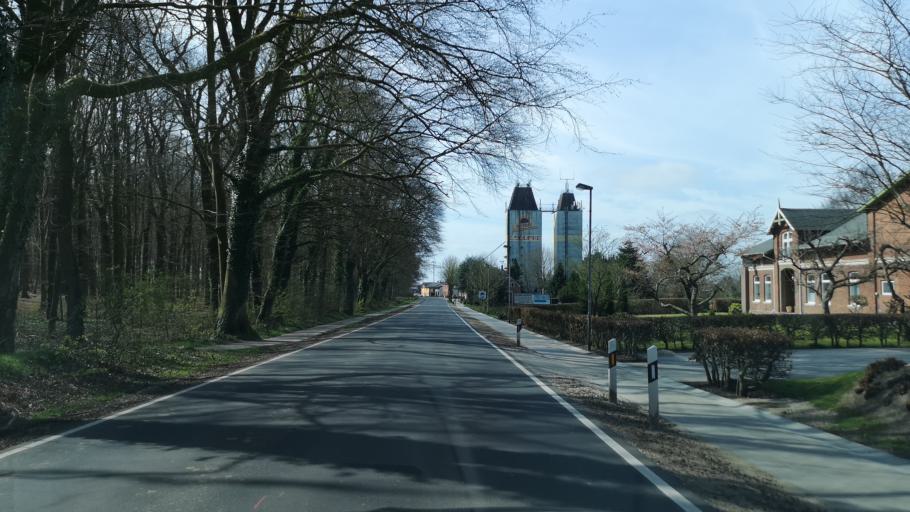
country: DE
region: Schleswig-Holstein
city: Albersdorf
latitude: 54.1512
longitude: 9.2908
